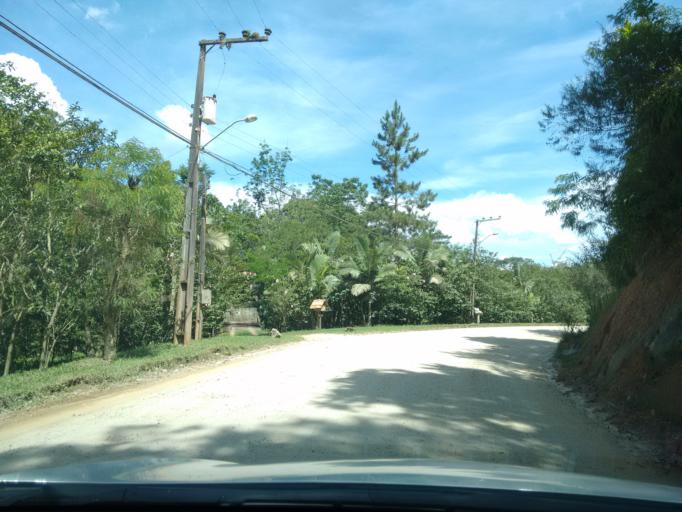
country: BR
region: Santa Catarina
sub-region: Pomerode
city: Pomerode
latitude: -26.6967
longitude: -49.1075
